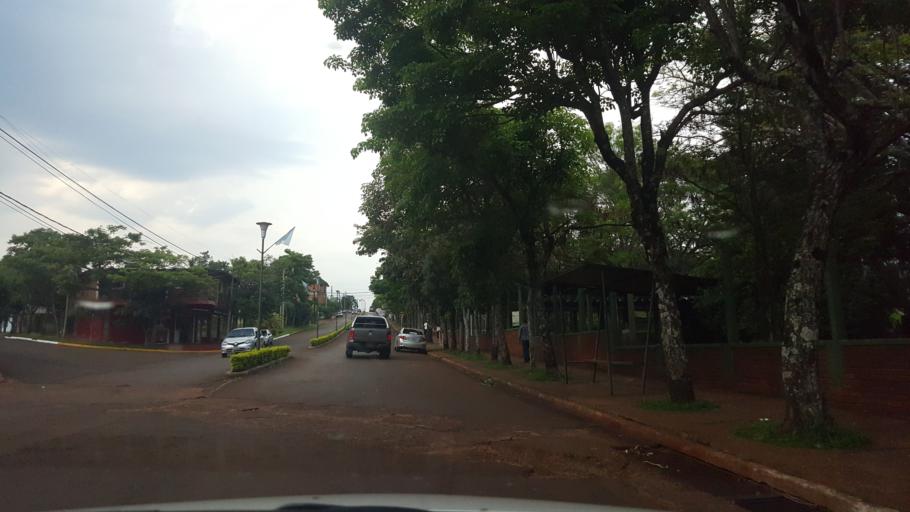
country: AR
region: Misiones
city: Capiovi
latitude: -26.9307
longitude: -55.0578
